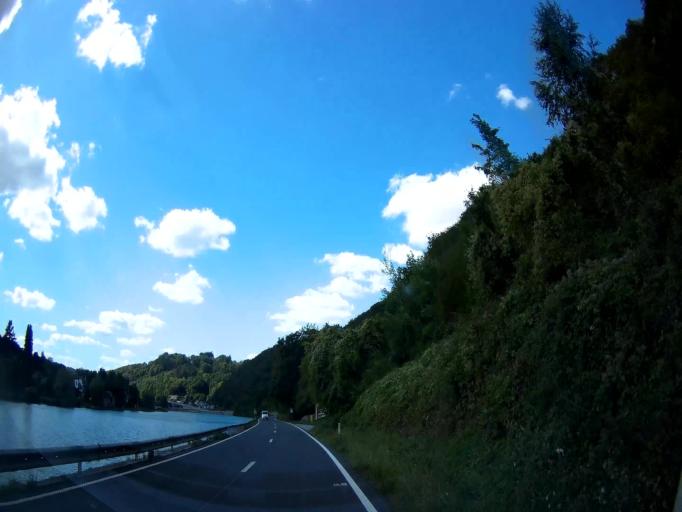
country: BE
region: Wallonia
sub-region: Province de Namur
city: Hastiere-Lavaux
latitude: 50.2166
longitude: 4.8378
